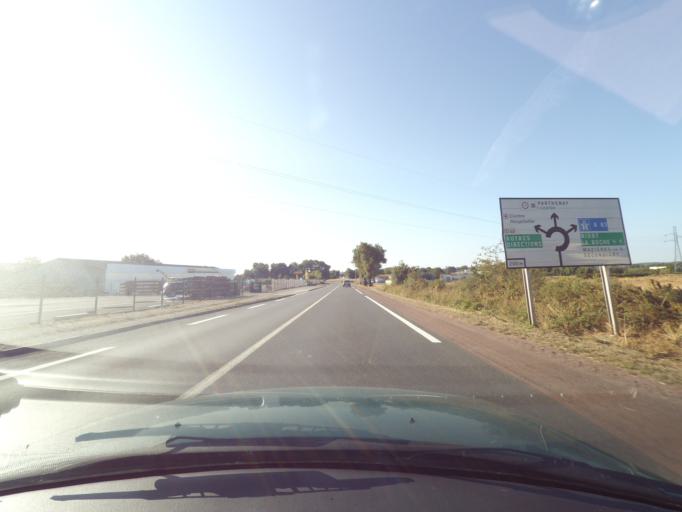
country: FR
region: Poitou-Charentes
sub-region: Departement des Deux-Sevres
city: Parthenay
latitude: 46.6666
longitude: -0.2530
